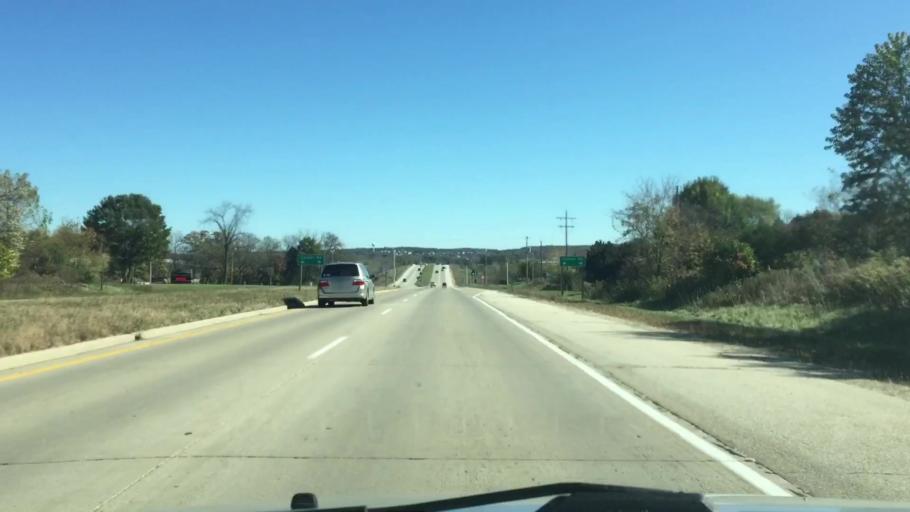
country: US
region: Wisconsin
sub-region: Waukesha County
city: Waukesha
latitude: 42.9769
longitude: -88.2505
